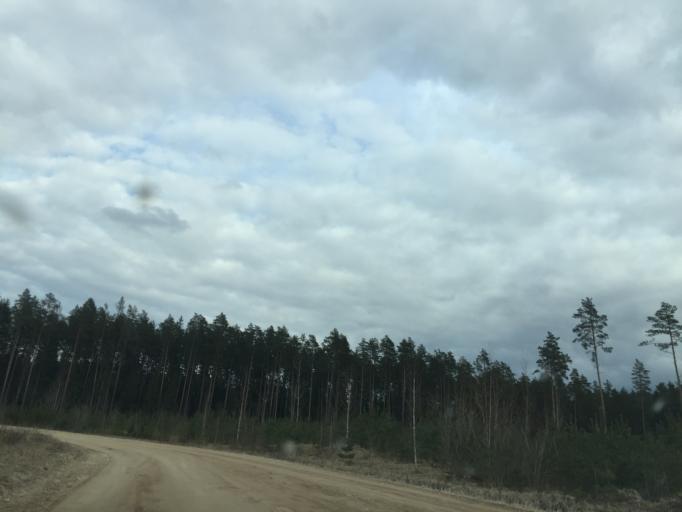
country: LV
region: Lielvarde
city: Lielvarde
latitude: 56.5307
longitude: 24.7993
